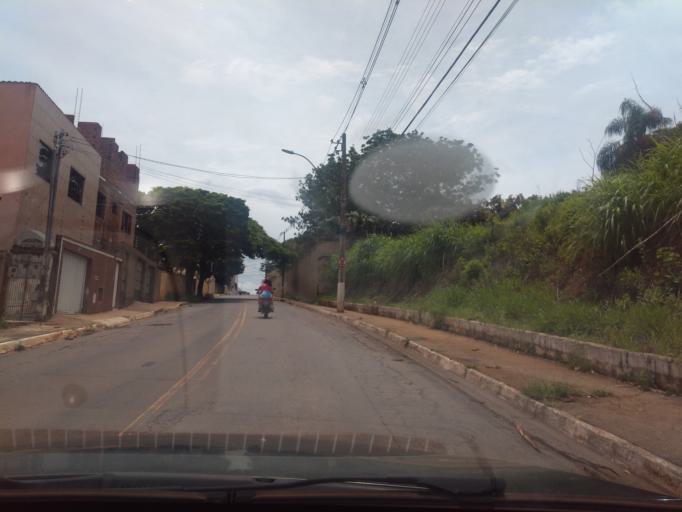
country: BR
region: Minas Gerais
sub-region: Tres Coracoes
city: Tres Coracoes
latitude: -21.6891
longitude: -45.2563
